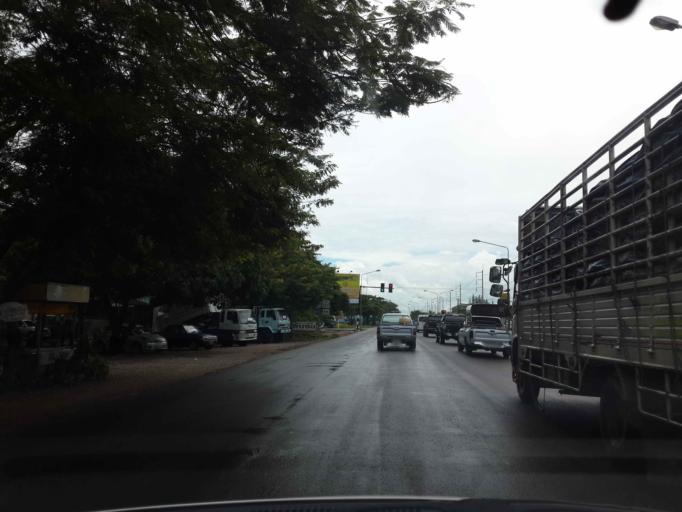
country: TH
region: Ratchaburi
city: Ratchaburi
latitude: 13.4568
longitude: 99.7999
